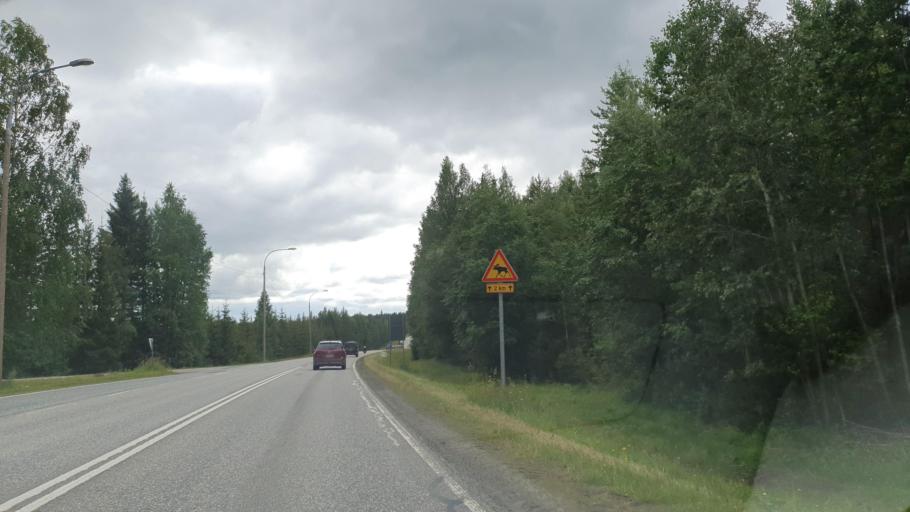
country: FI
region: Northern Savo
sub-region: Ylae-Savo
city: Sonkajaervi
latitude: 63.6961
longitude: 27.3556
